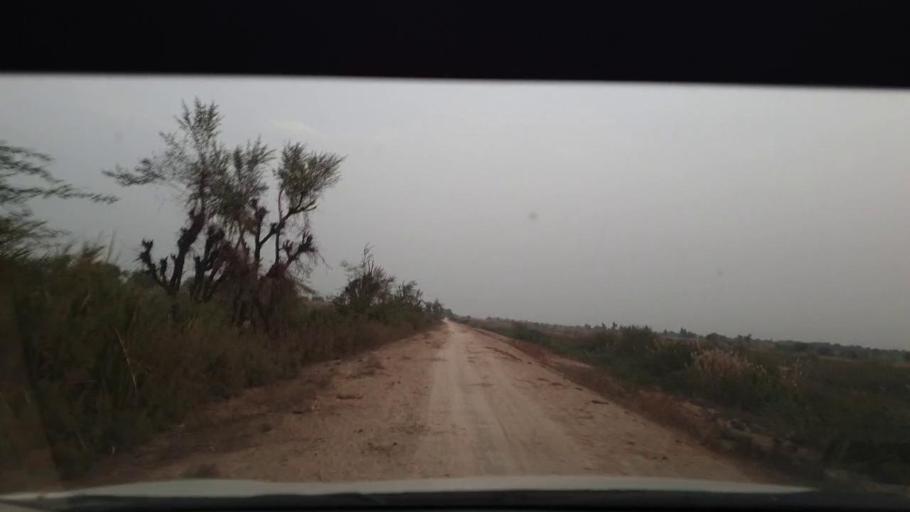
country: PK
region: Sindh
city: Berani
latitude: 25.8552
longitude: 68.7799
